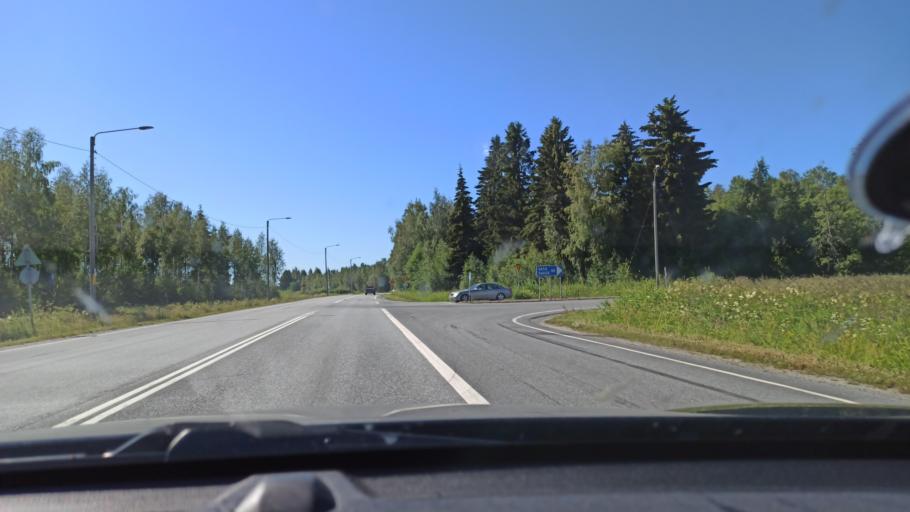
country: FI
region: Ostrobothnia
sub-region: Jakobstadsregionen
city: Bennaes
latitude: 63.6073
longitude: 22.7798
